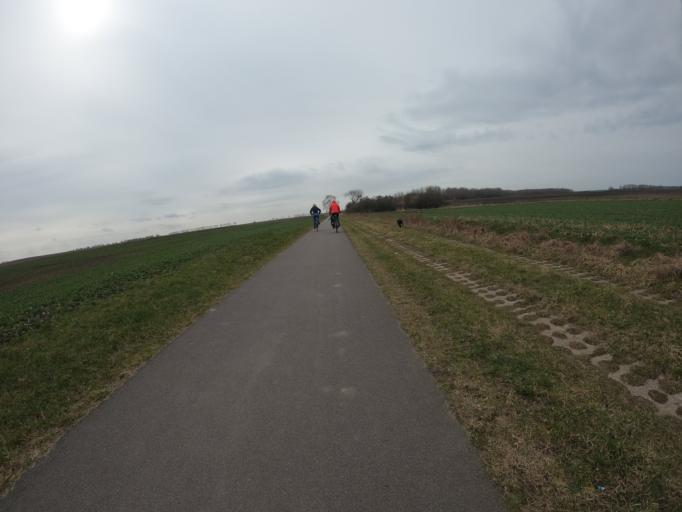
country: PL
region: West Pomeranian Voivodeship
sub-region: Powiat gryficki
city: Mrzezyno
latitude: 54.1125
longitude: 15.2985
